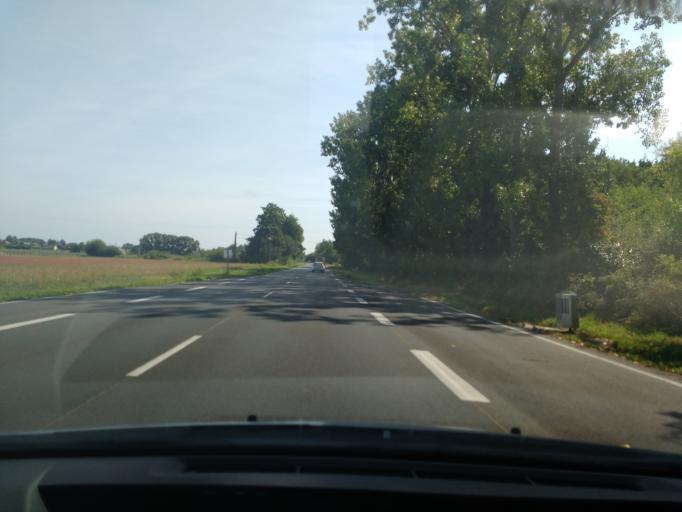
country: FR
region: Pays de la Loire
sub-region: Departement de Maine-et-Loire
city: Andard
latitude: 47.4652
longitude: -0.3940
